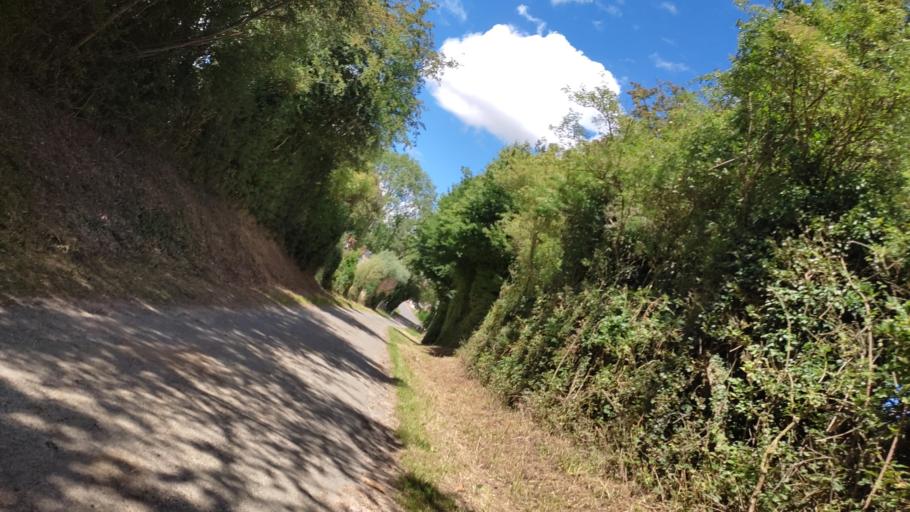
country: FR
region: Nord-Pas-de-Calais
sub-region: Departement du Pas-de-Calais
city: Beaumetz-les-Loges
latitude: 50.2235
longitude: 2.6462
